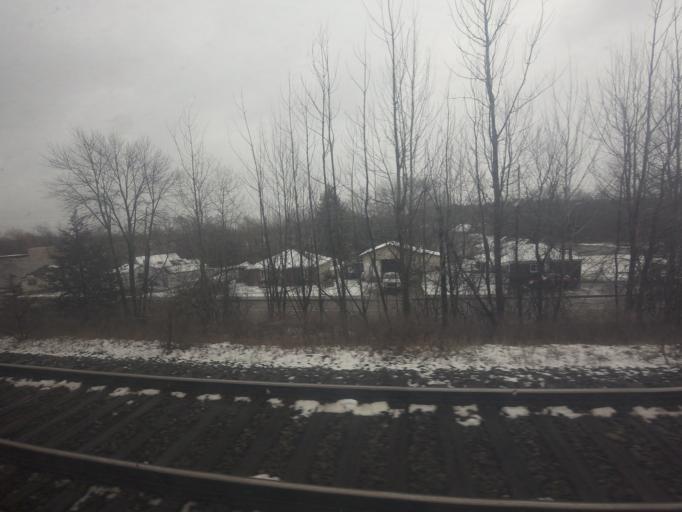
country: CA
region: Ontario
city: Quinte West
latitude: 44.1121
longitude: -77.6014
